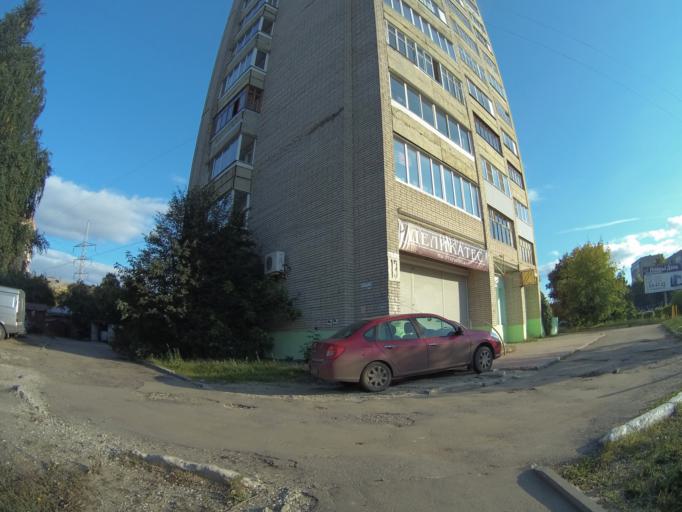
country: RU
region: Vladimir
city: Vladimir
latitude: 56.1125
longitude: 40.3452
